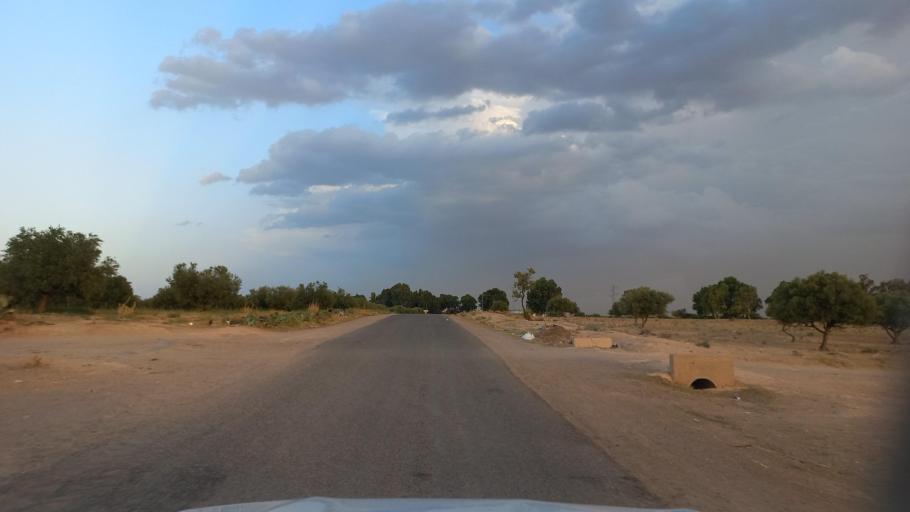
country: TN
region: Al Qasrayn
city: Kasserine
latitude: 35.2714
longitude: 9.0720
